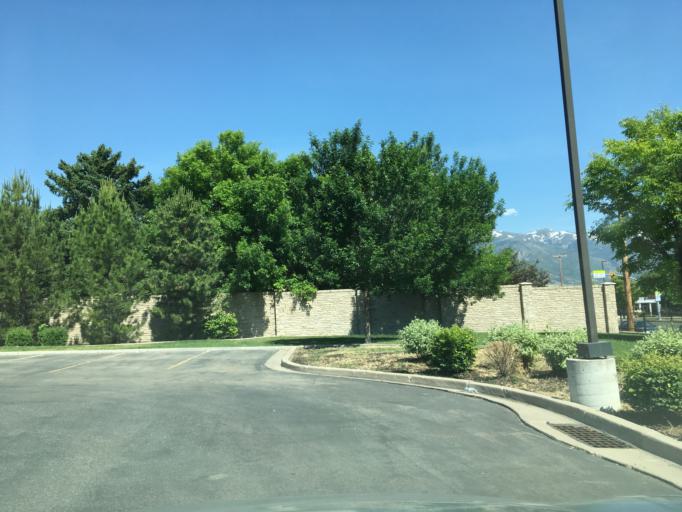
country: US
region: Utah
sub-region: Davis County
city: Hill Air Force Bace
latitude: 41.0894
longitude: -111.9786
